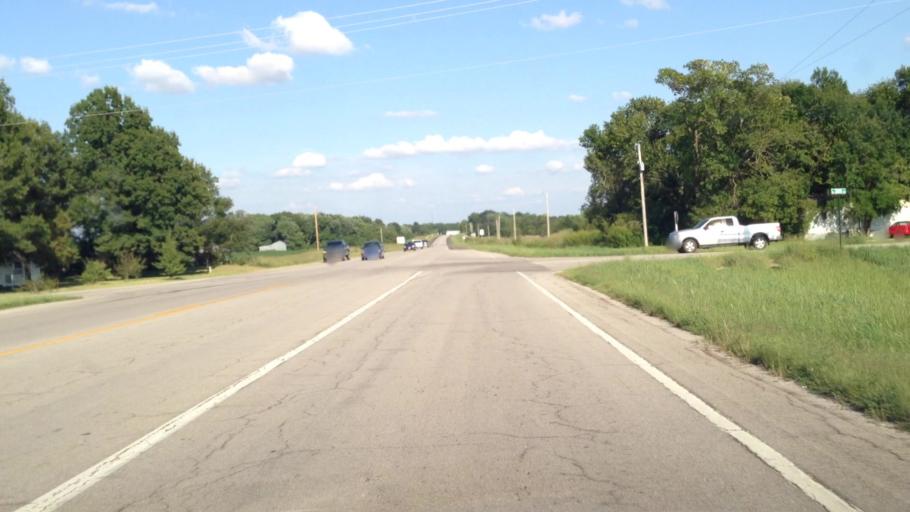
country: US
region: Kansas
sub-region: Crawford County
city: Frontenac
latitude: 37.4692
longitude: -94.6313
